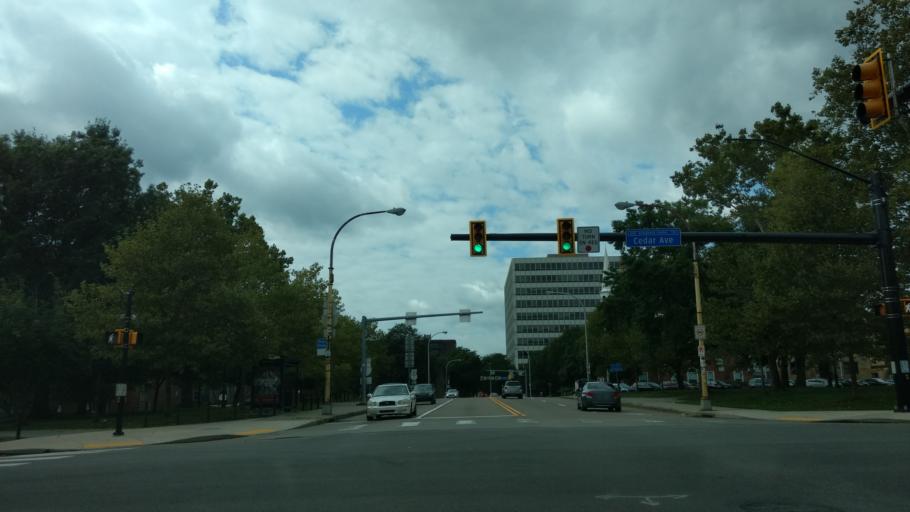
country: US
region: Pennsylvania
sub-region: Allegheny County
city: Pittsburgh
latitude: 40.4534
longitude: -80.0016
